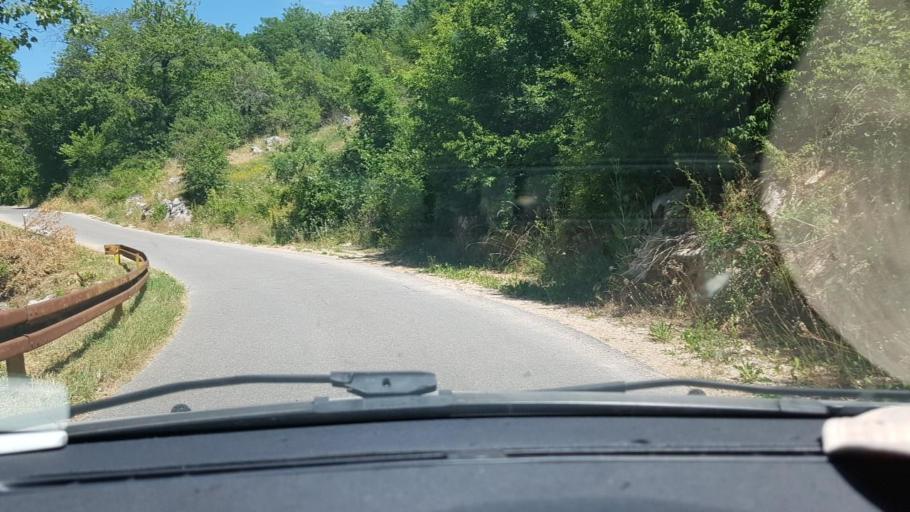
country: HR
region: Licko-Senjska
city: Otocac
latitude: 44.7891
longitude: 15.3687
